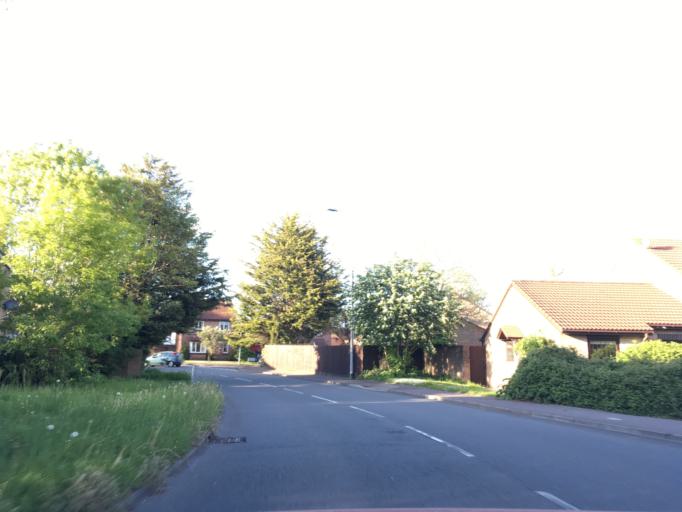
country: GB
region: Wales
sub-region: Newport
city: Marshfield
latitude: 51.5273
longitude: -3.0938
